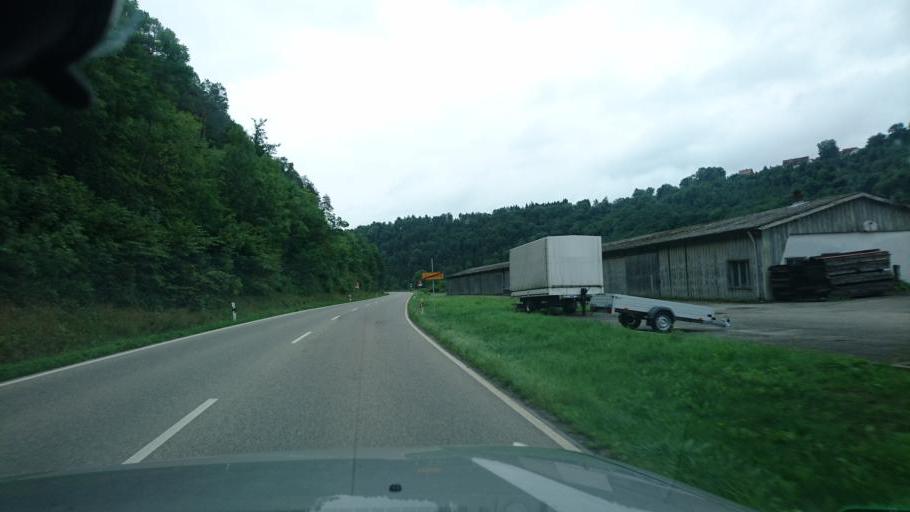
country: DE
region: Baden-Wuerttemberg
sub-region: Freiburg Region
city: Sulz am Neckar
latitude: 48.3712
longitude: 8.6478
